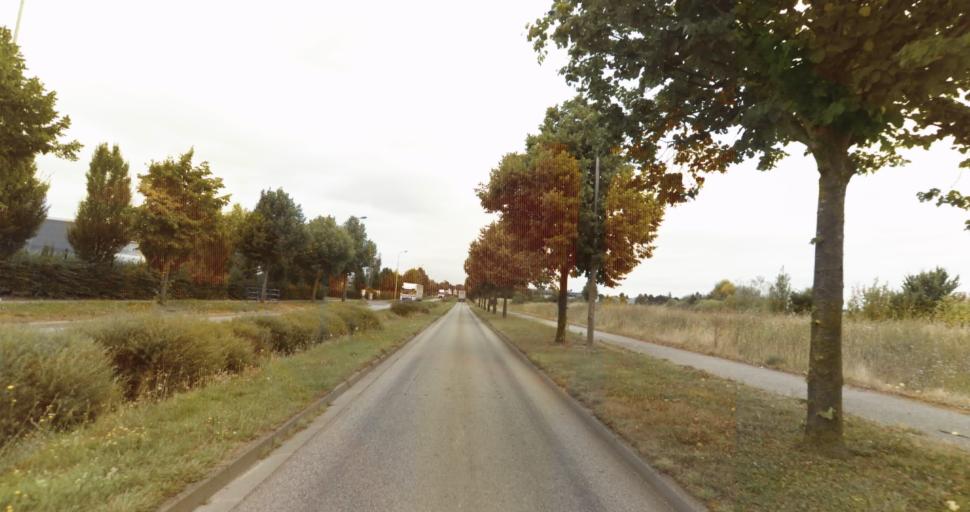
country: FR
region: Haute-Normandie
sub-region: Departement de l'Eure
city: Evreux
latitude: 49.0112
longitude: 1.1852
